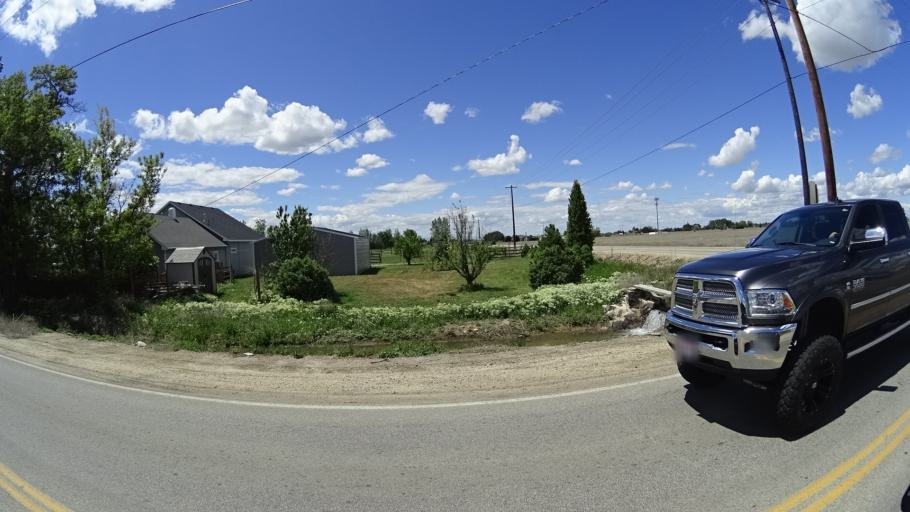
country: US
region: Idaho
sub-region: Ada County
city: Meridian
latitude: 43.5609
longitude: -116.4338
